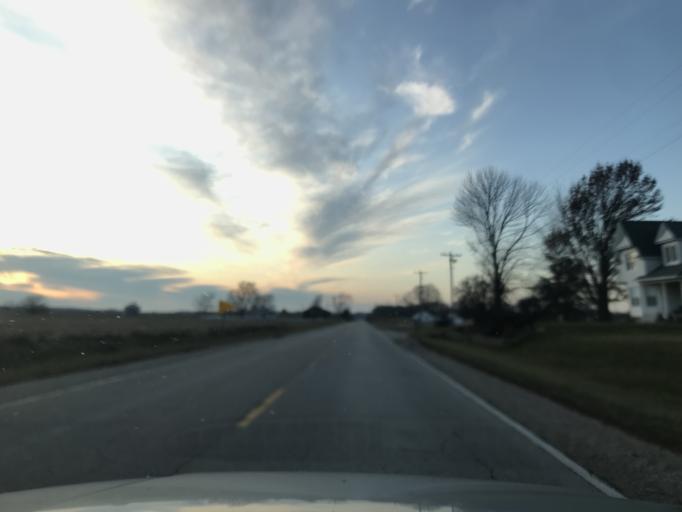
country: US
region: Illinois
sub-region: Henderson County
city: Oquawka
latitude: 41.0184
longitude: -90.7985
